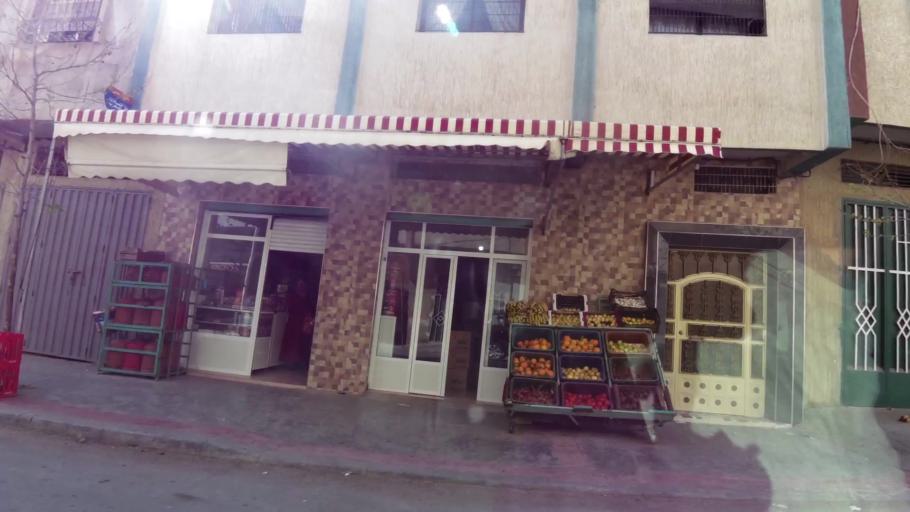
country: MA
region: Tanger-Tetouan
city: Tetouan
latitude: 35.5877
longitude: -5.3589
